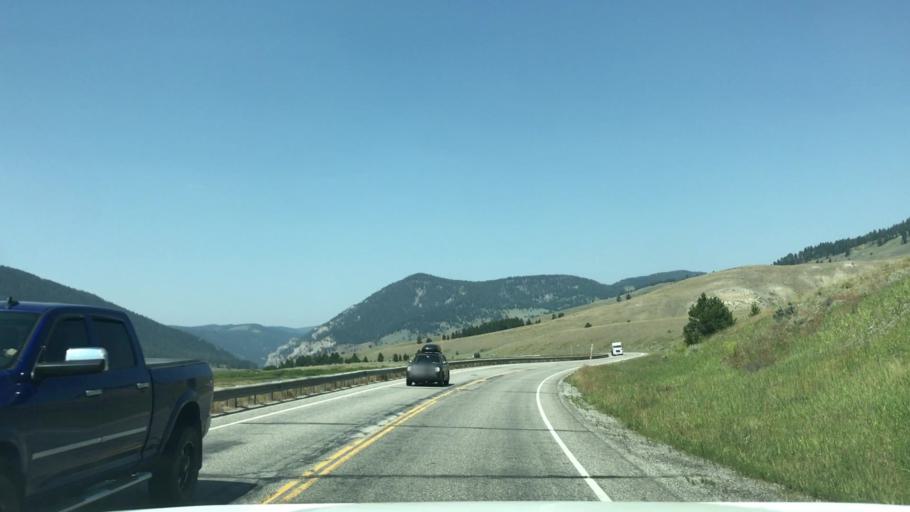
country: US
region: Montana
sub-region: Gallatin County
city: Big Sky
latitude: 45.0432
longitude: -111.1309
